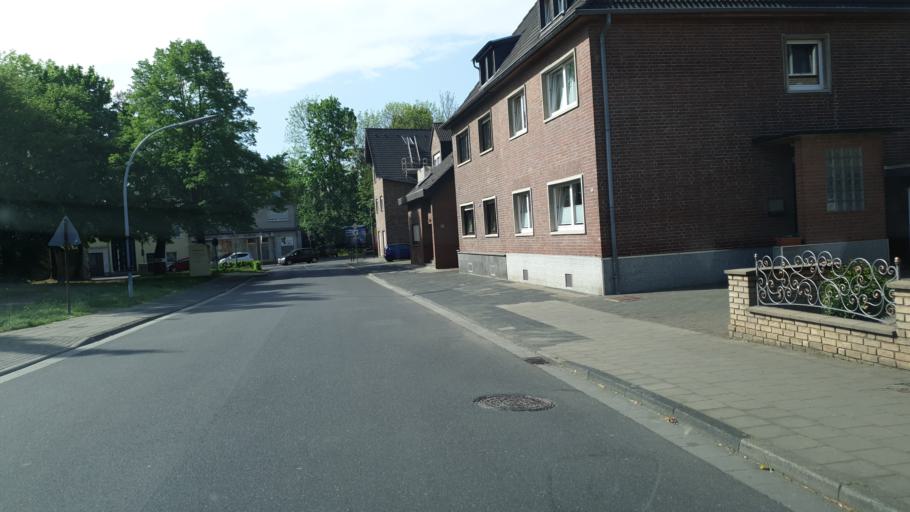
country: DE
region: North Rhine-Westphalia
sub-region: Regierungsbezirk Koln
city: Bergheim
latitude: 50.9406
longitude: 6.6770
